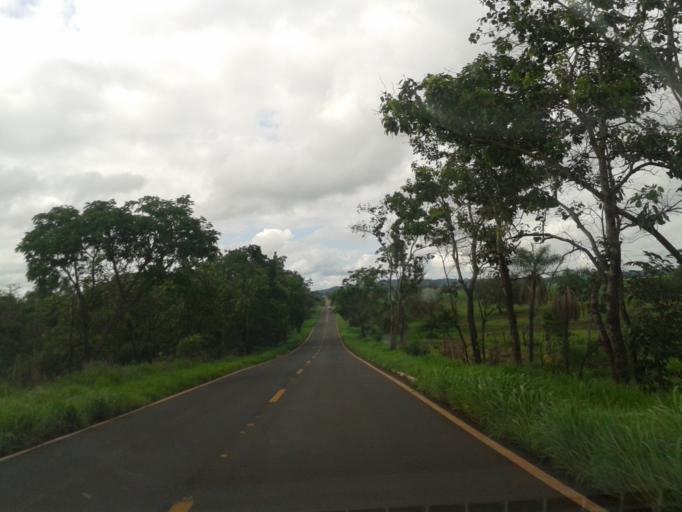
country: BR
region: Minas Gerais
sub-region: Ituiutaba
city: Ituiutaba
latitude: -19.1303
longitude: -49.7737
